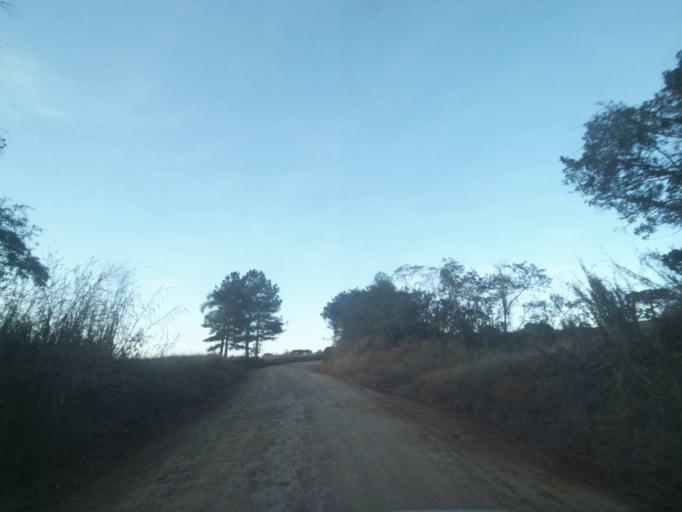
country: BR
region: Parana
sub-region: Tibagi
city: Tibagi
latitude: -24.5233
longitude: -50.5051
